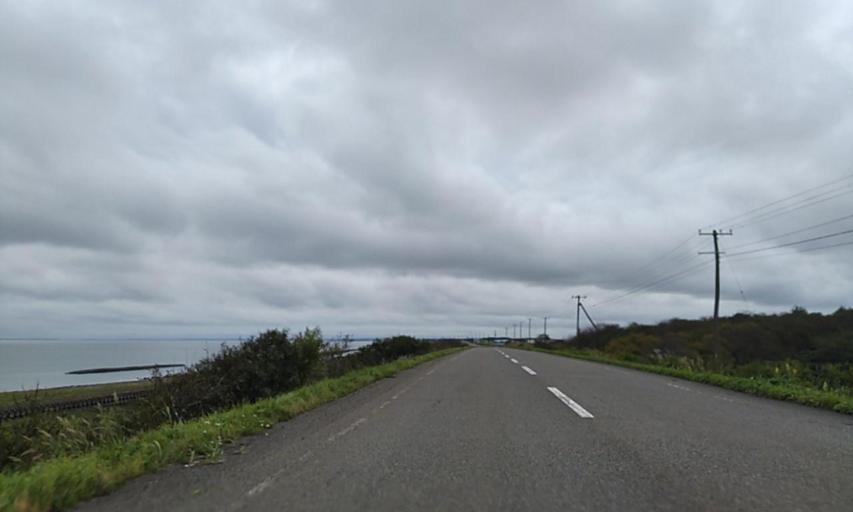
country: JP
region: Hokkaido
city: Shibetsu
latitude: 43.4265
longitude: 145.2661
